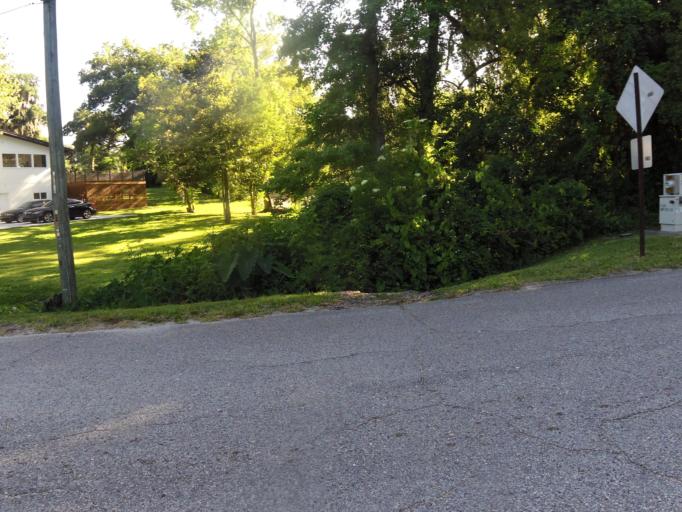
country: US
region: Florida
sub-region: Duval County
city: Jacksonville
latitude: 30.3131
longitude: -81.6174
